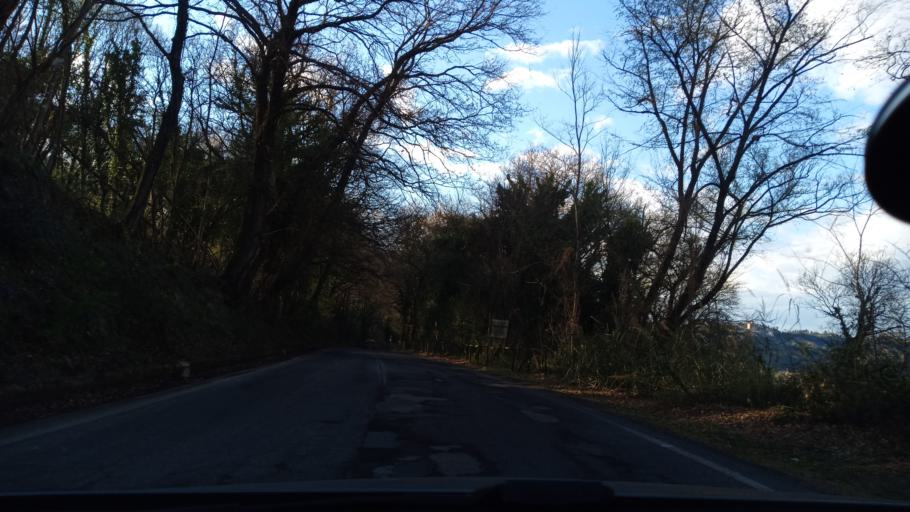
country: IT
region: Latium
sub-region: Citta metropolitana di Roma Capitale
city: Nazzano
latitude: 42.2075
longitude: 12.6049
